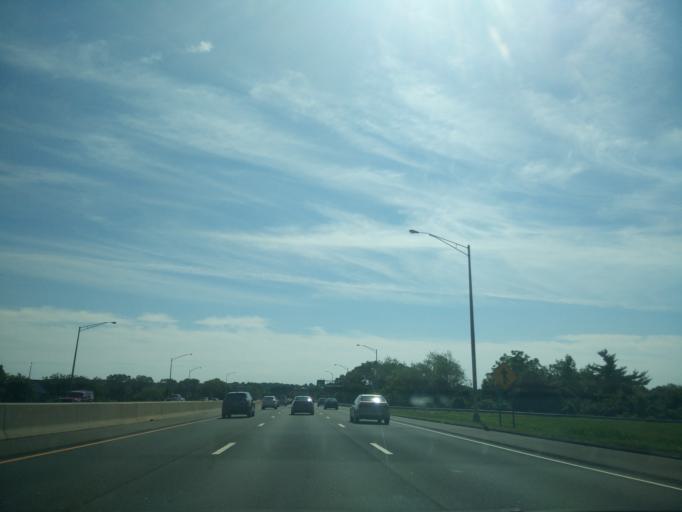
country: US
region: Connecticut
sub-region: New Haven County
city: Milford
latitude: 41.2349
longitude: -73.0448
